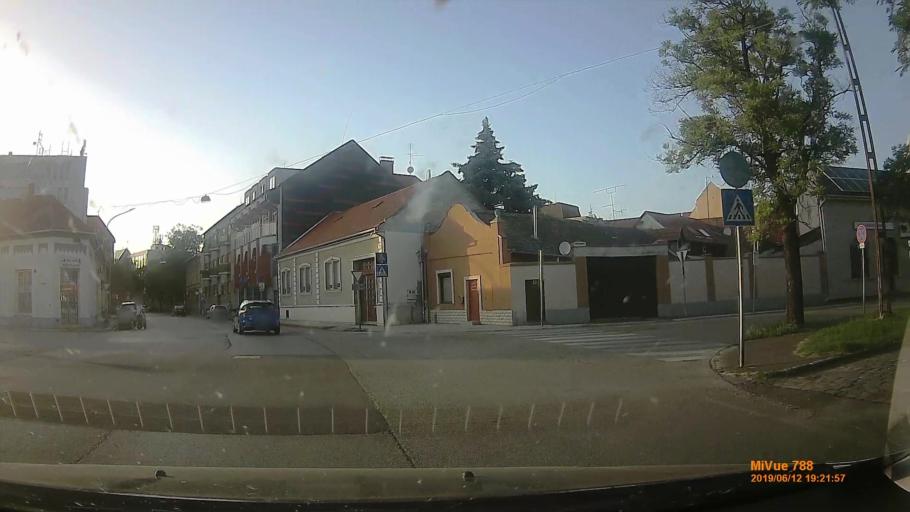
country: HU
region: Bacs-Kiskun
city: Kecskemet
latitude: 46.9066
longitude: 19.6966
